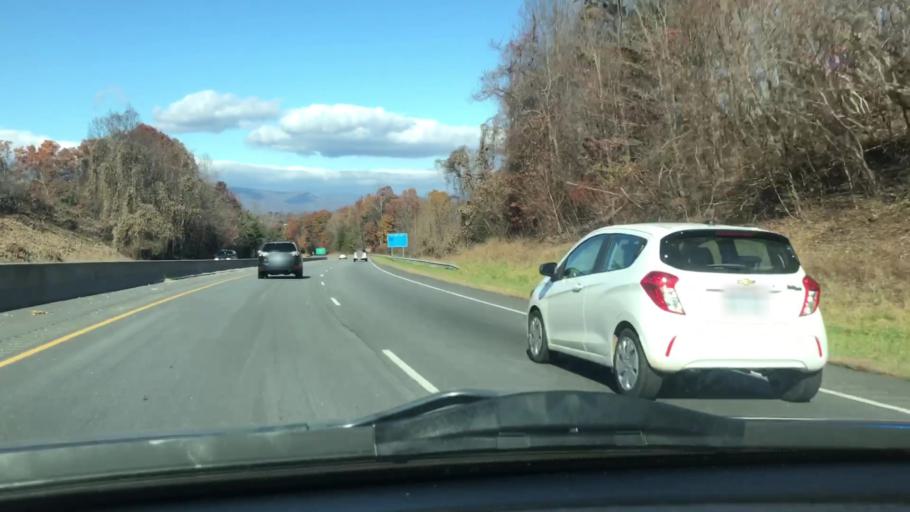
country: US
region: North Carolina
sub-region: McDowell County
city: Marion
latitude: 35.6678
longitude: -82.0108
